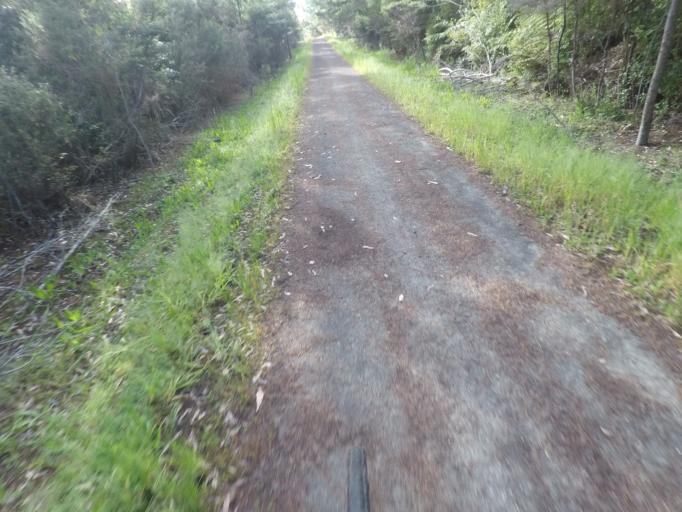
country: NZ
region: Auckland
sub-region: Auckland
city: Parakai
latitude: -36.7083
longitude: 174.5807
